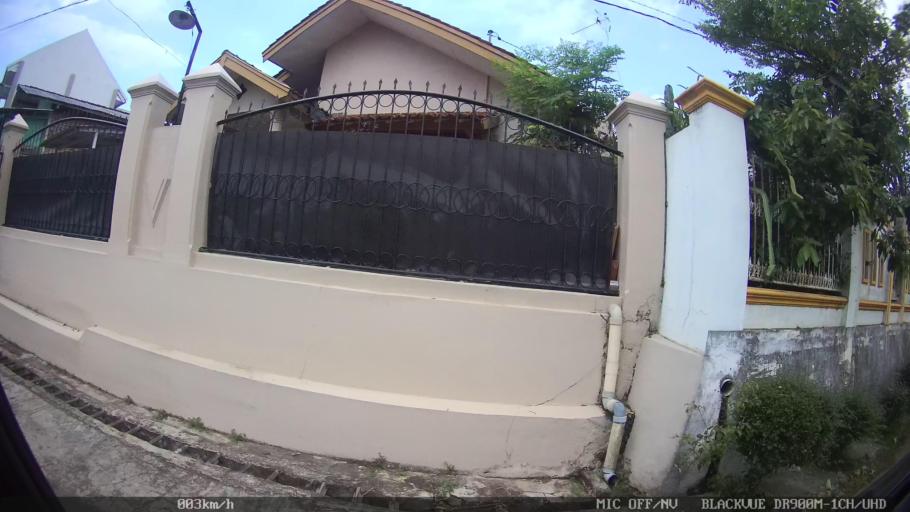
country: ID
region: Lampung
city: Kedaton
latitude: -5.3931
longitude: 105.2074
